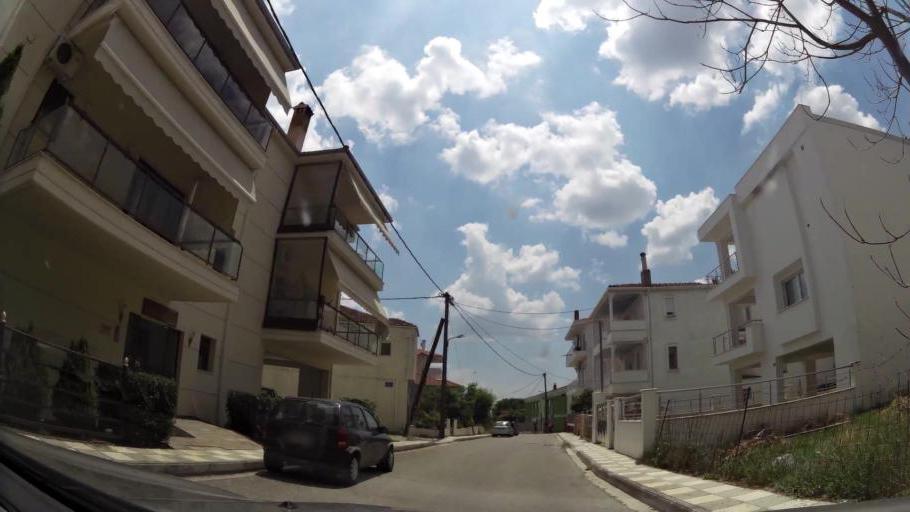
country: GR
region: West Macedonia
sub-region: Nomos Kozanis
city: Kozani
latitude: 40.2912
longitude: 21.7868
